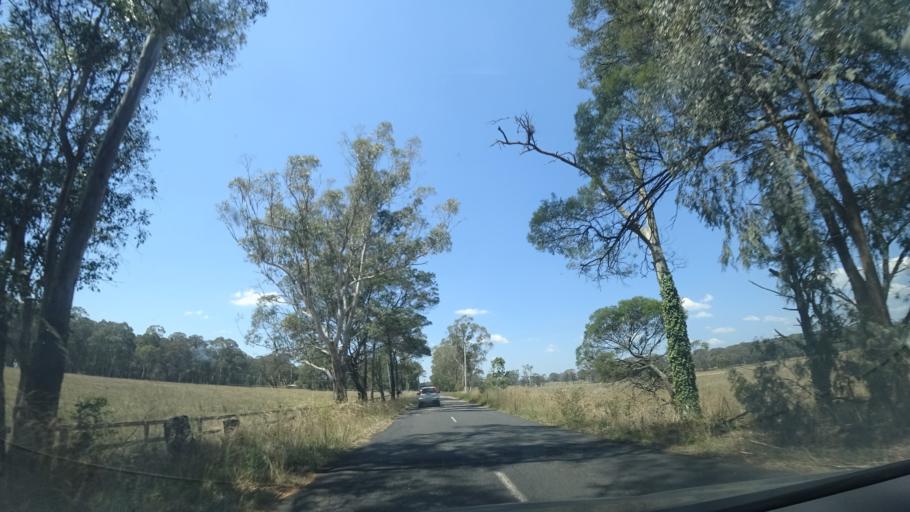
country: AU
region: New South Wales
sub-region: Wingecarribee
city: Bundanoon
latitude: -34.6111
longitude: 150.2582
